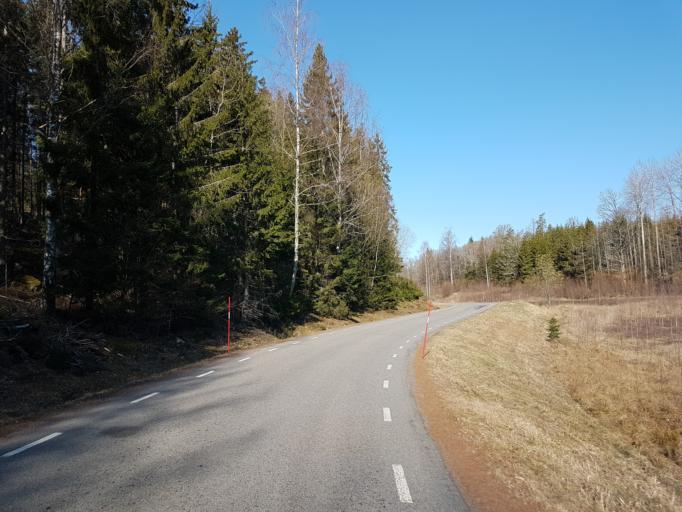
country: SE
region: OEstergoetland
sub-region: Valdemarsviks Kommun
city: Gusum
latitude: 58.1891
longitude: 16.3000
